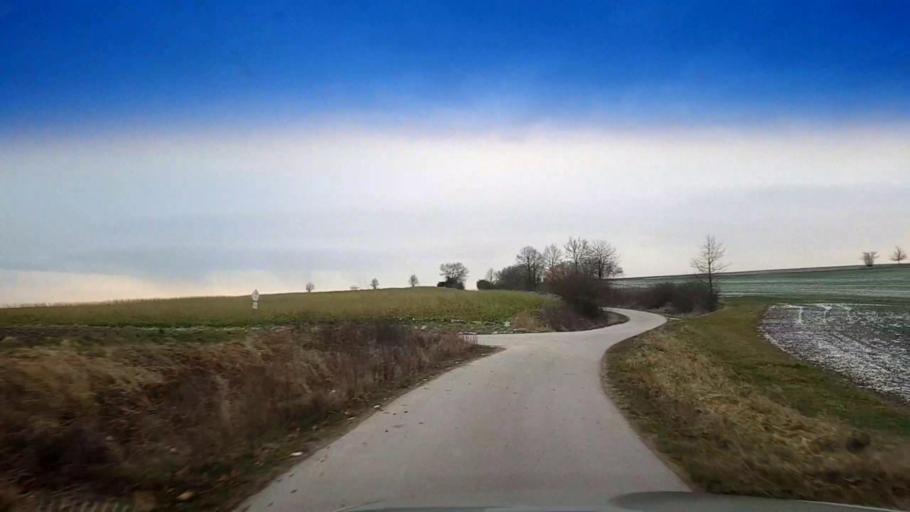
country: DE
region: Bavaria
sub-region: Upper Franconia
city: Frensdorf
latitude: 49.8135
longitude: 10.8199
